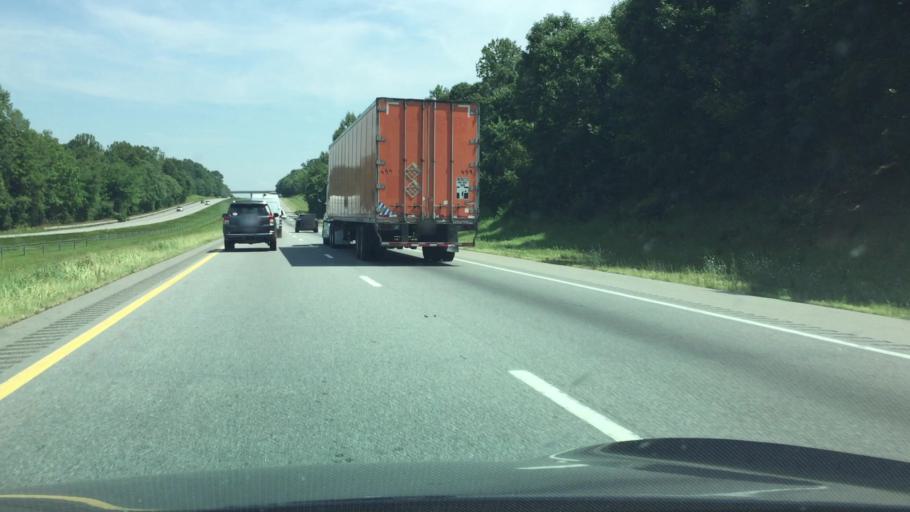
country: US
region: North Carolina
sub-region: Yadkin County
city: Yadkinville
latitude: 36.0606
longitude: -80.8223
